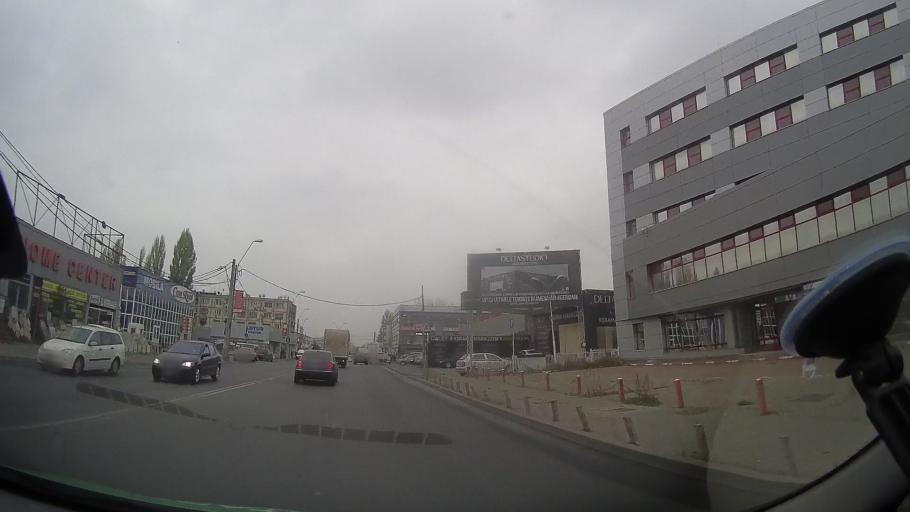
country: RO
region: Ilfov
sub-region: Comuna Chiajna
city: Rosu
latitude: 44.4300
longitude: 26.0031
